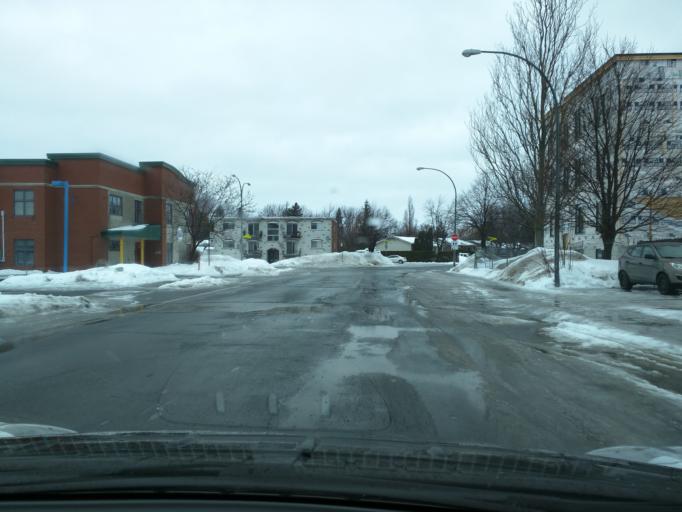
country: CA
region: Quebec
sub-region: Monteregie
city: Longueuil
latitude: 45.5260
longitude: -73.4596
